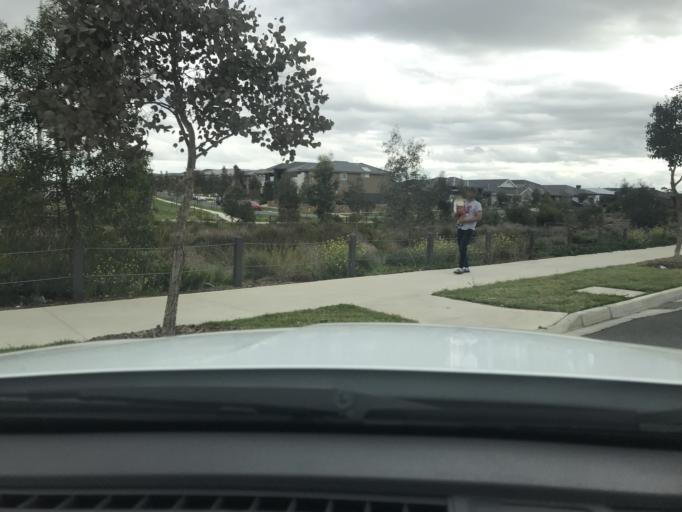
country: AU
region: Victoria
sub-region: Hume
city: Greenvale
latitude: -37.5944
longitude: 144.8906
